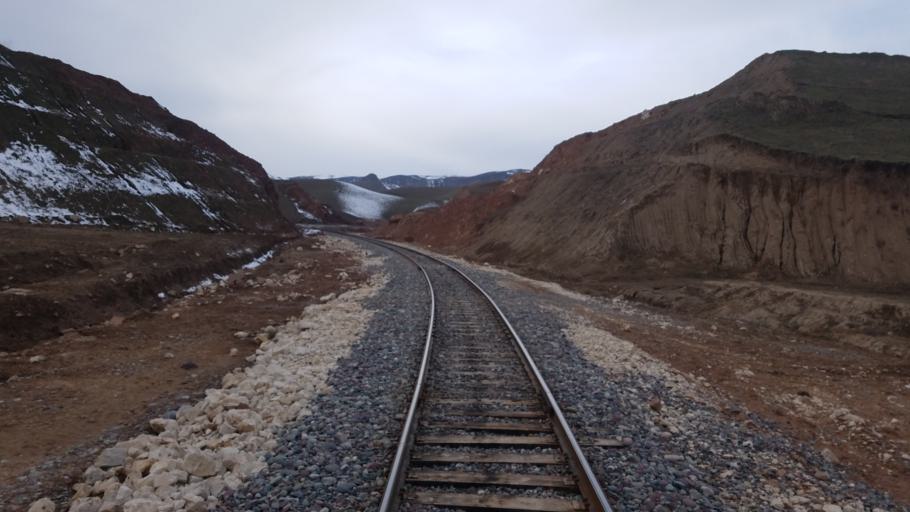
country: TJ
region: Khatlon
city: Yovon
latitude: 38.3712
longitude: 68.9420
